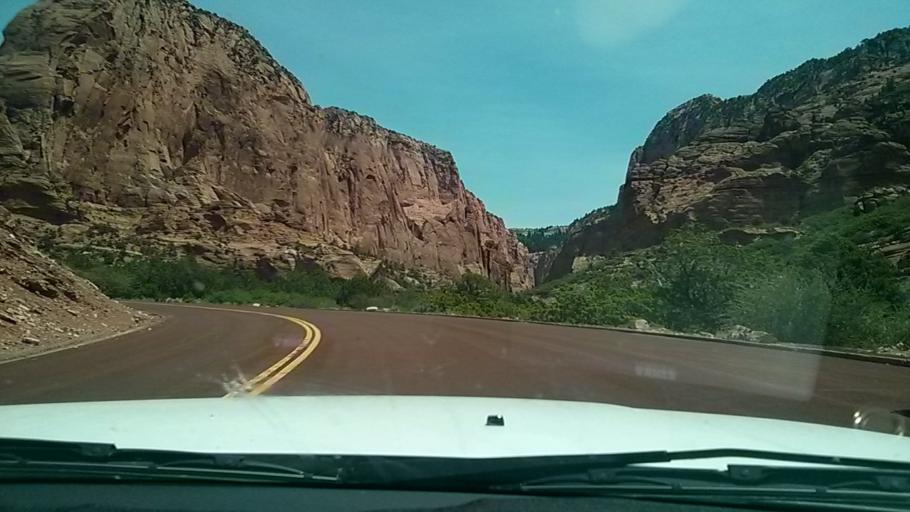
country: US
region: Utah
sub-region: Washington County
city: Toquerville
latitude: 37.4544
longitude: -113.1885
